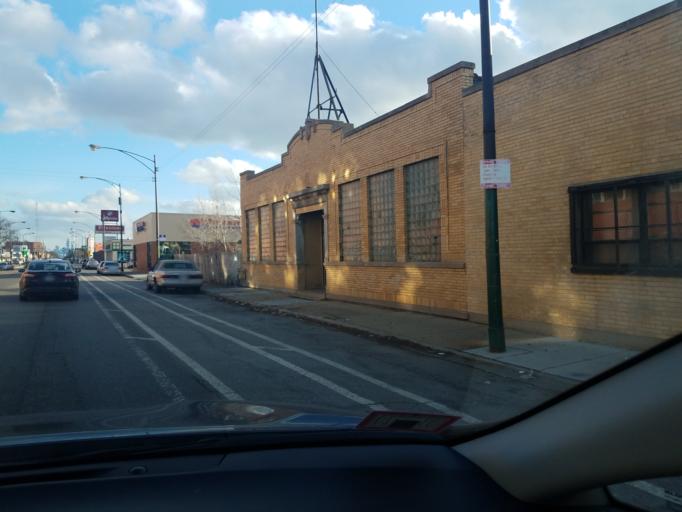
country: US
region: Illinois
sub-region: Cook County
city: Lincolnwood
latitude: 41.9480
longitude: -87.7109
